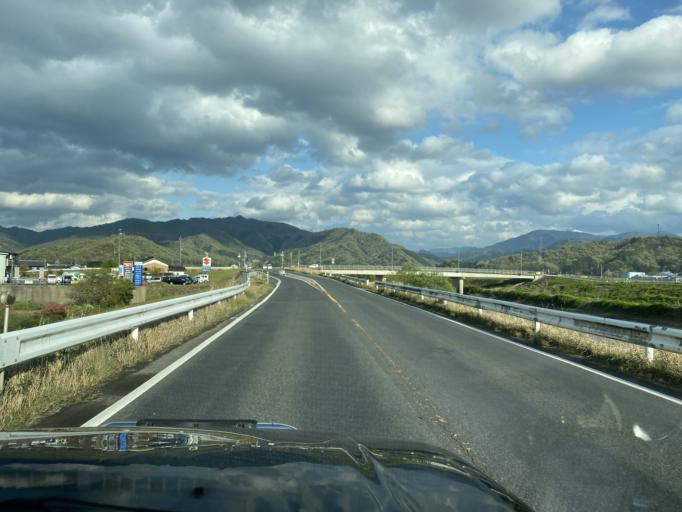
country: JP
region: Hyogo
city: Toyooka
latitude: 35.4898
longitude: 134.8465
